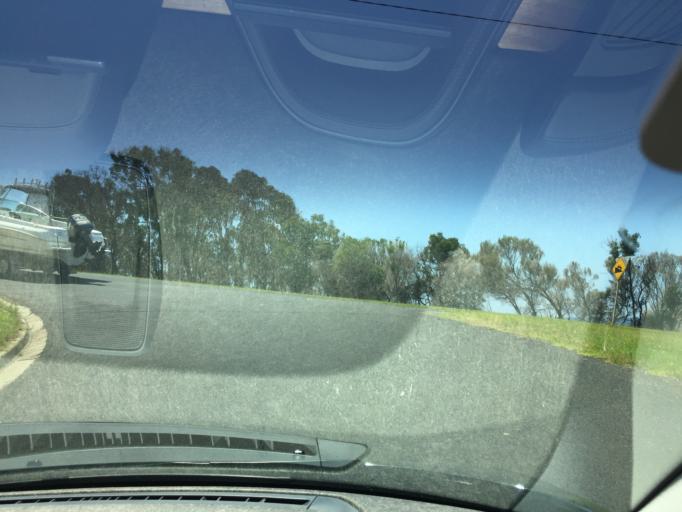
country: AU
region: New South Wales
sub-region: Bega Valley
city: Bega
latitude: -36.7357
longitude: 149.9833
